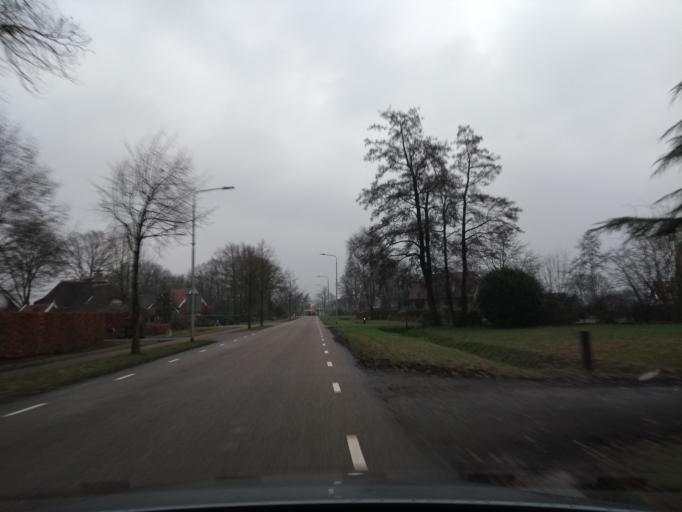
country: NL
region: Overijssel
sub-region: Gemeente Twenterand
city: Westerhaar-Vriezenveensewijk
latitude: 52.4356
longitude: 6.6695
